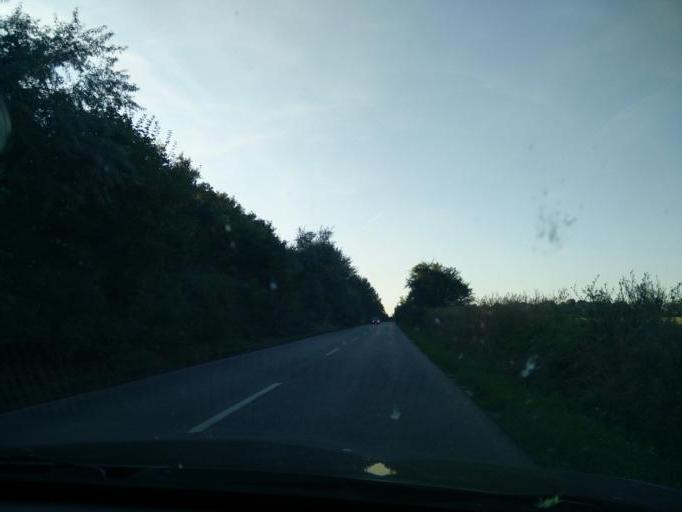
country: HU
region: Pest
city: Perbal
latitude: 47.6091
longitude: 18.7710
